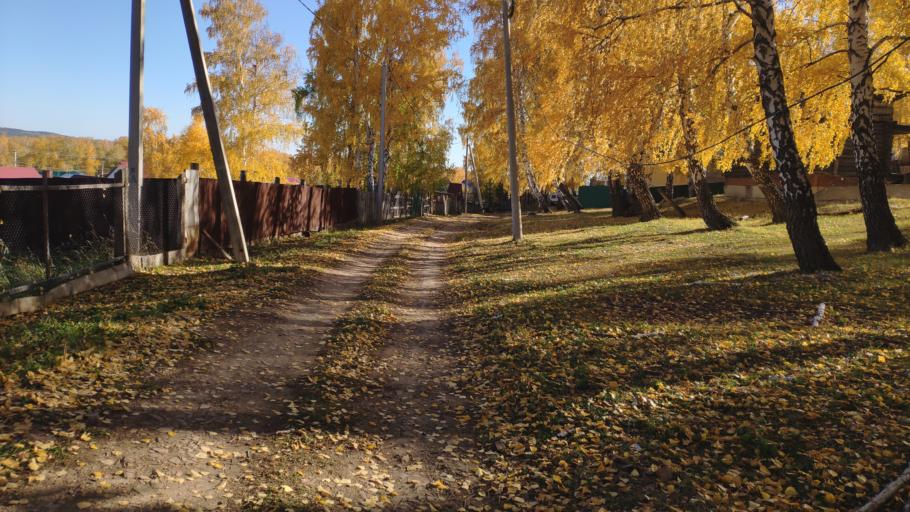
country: RU
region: Bashkortostan
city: Abzakovo
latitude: 53.3444
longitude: 58.5028
